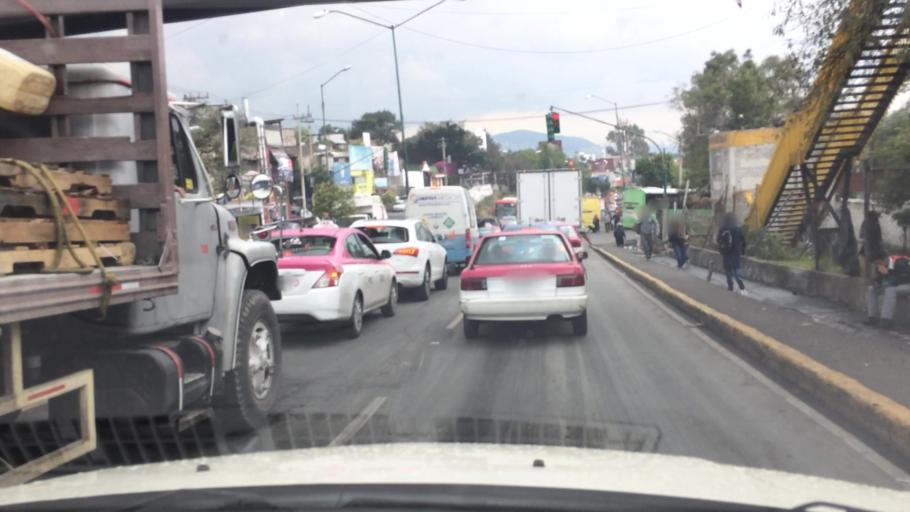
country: MX
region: Mexico City
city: Magdalena Contreras
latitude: 19.2834
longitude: -99.2171
